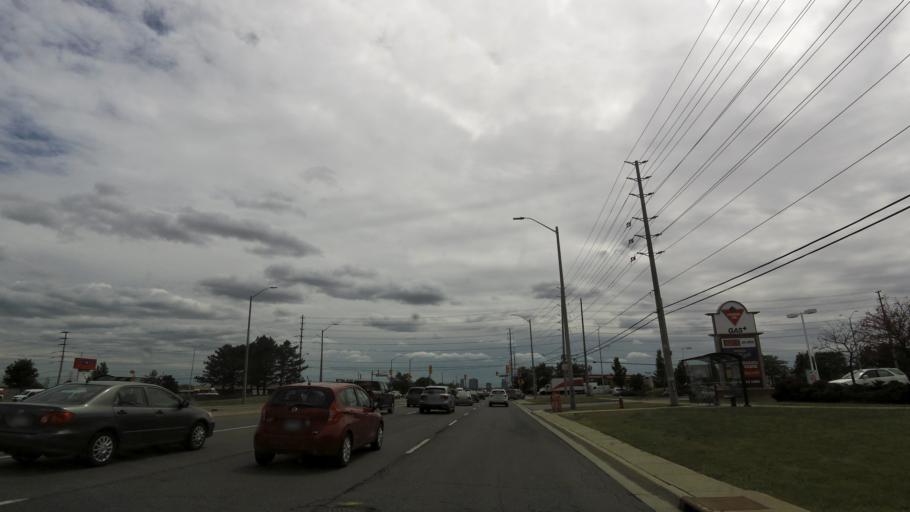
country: CA
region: Ontario
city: Etobicoke
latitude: 43.6366
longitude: -79.6200
